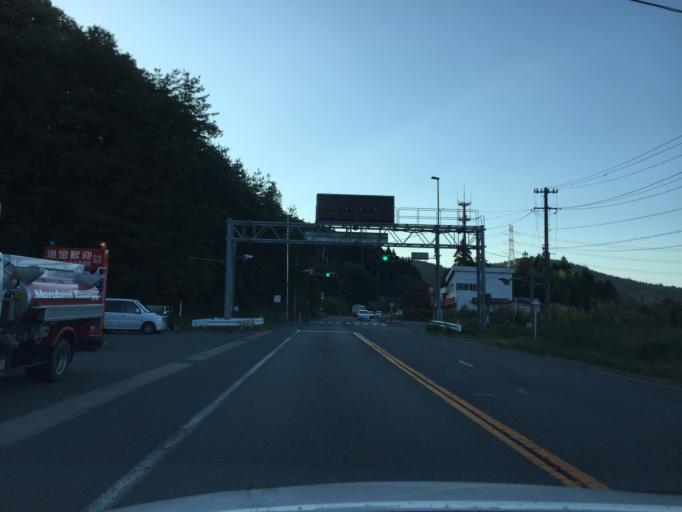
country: JP
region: Fukushima
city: Ishikawa
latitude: 37.1923
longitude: 140.6343
